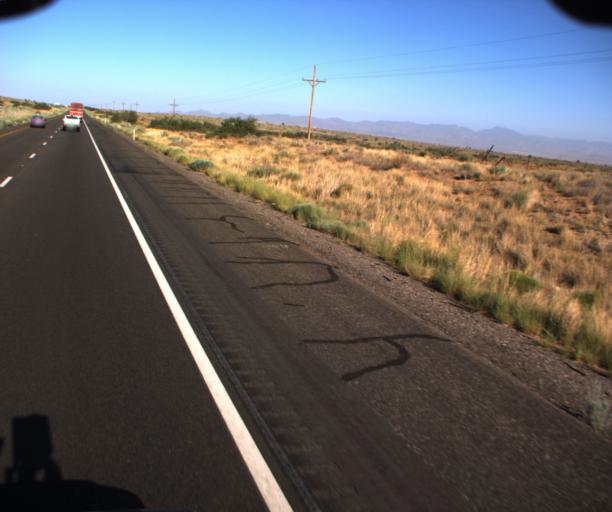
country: US
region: Arizona
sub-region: Mohave County
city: New Kingman-Butler
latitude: 35.1954
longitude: -113.8573
